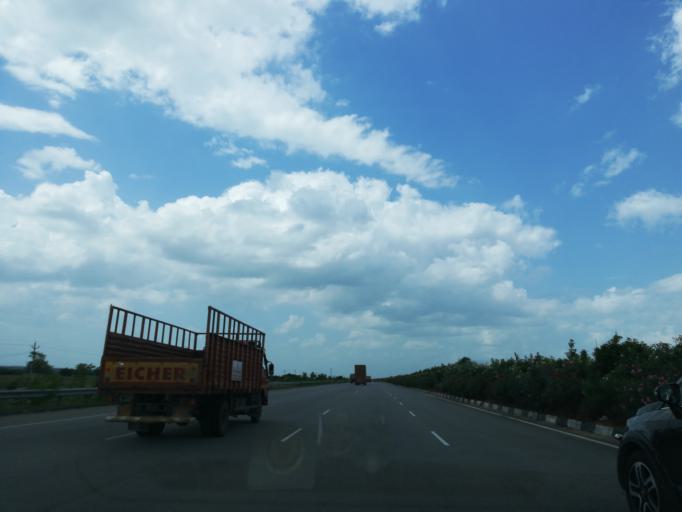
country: IN
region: Telangana
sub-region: Medak
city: Patancheru
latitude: 17.4884
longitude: 78.2457
